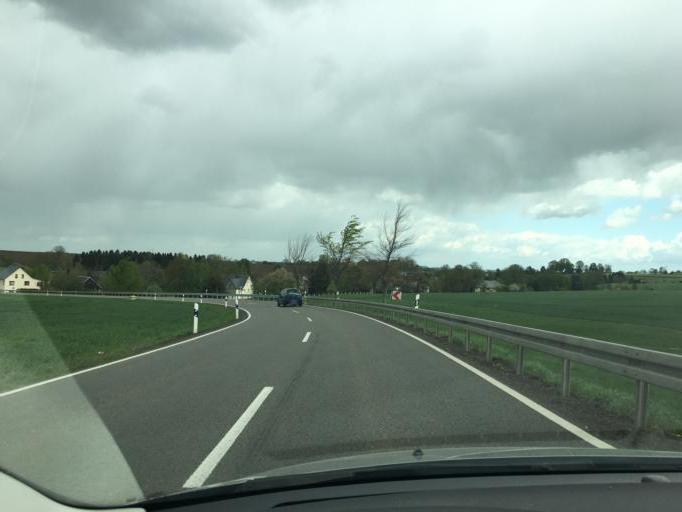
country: DE
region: Saxony
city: Limbach-Oberfrohna
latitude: 50.8269
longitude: 12.7560
